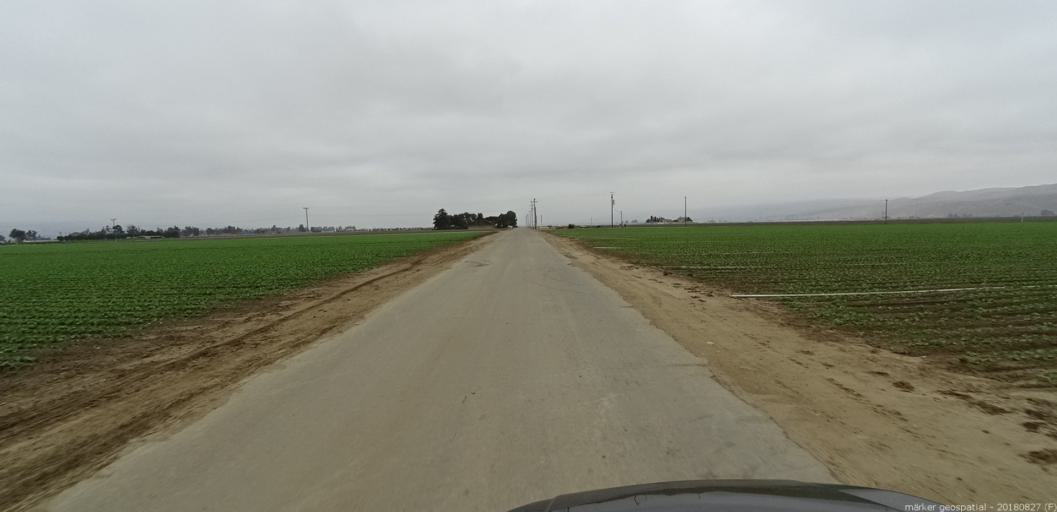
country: US
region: California
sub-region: Monterey County
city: Greenfield
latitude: 36.3336
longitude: -121.2406
